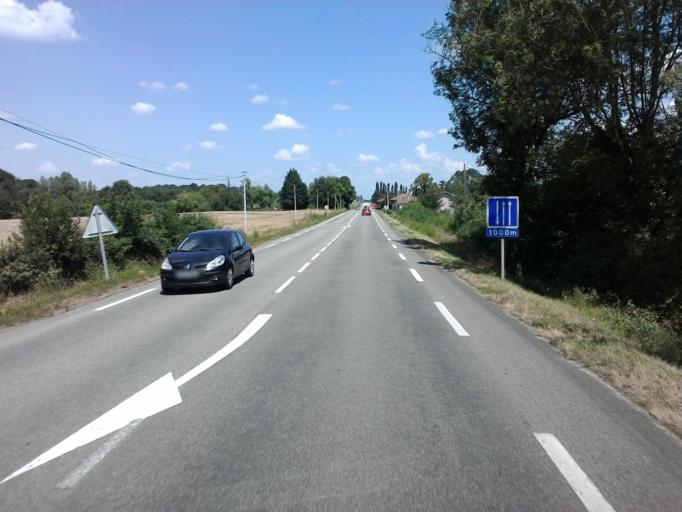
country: FR
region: Rhone-Alpes
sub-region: Departement de l'Ain
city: Saint-Etienne-du-Bois
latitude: 46.2960
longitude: 5.3002
